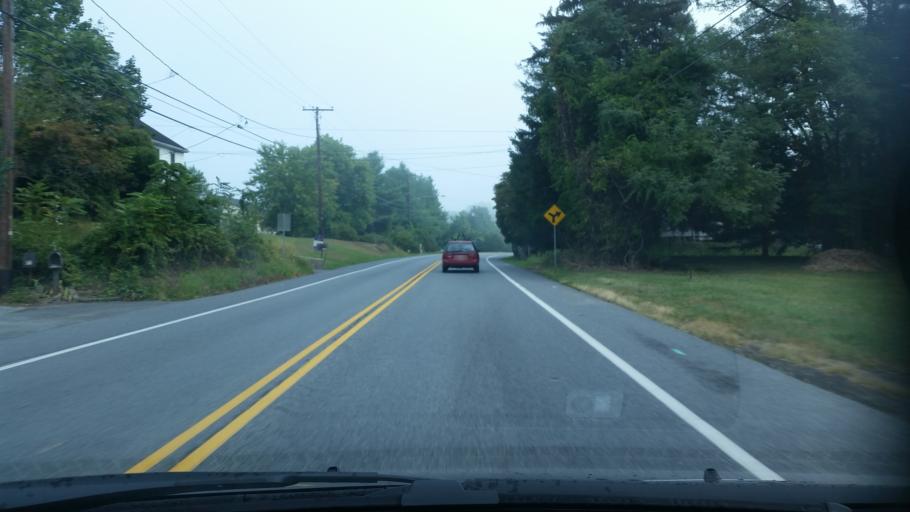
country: US
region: Pennsylvania
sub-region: Lancaster County
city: Lancaster
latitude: 40.0754
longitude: -76.2654
